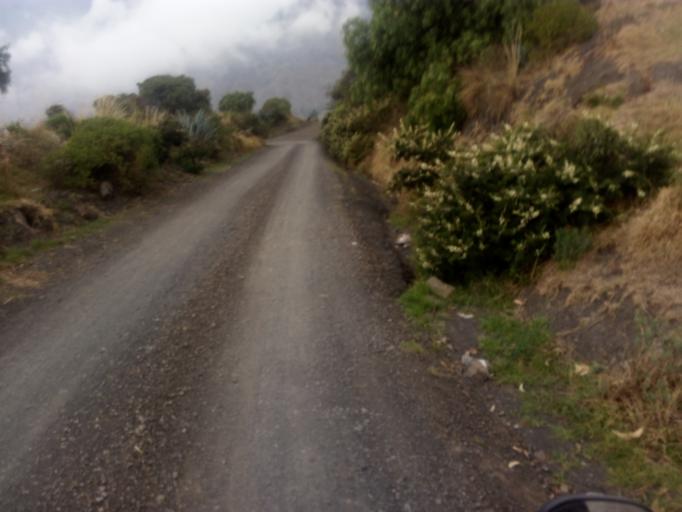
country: CO
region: Boyaca
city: Chita
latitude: 6.1933
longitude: -72.4887
